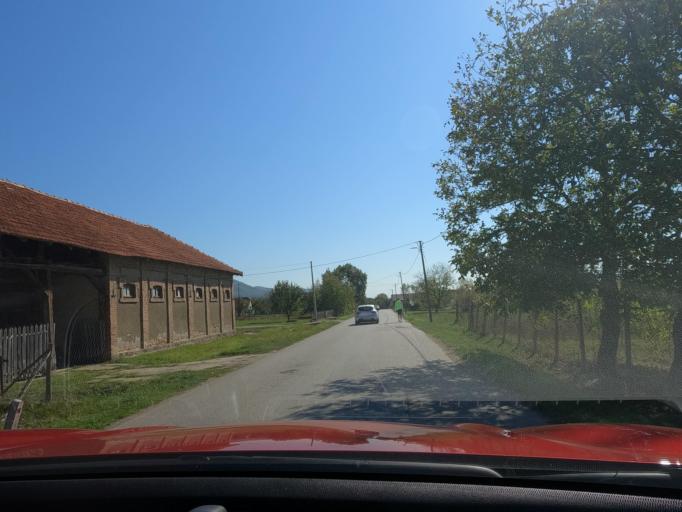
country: RS
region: Central Serbia
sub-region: Raski Okrug
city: Kraljevo
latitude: 43.7578
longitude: 20.6849
